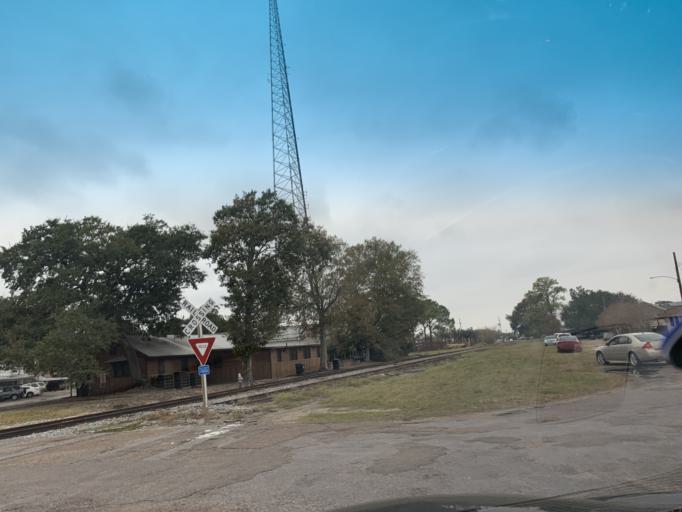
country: US
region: Louisiana
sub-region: Orleans Parish
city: New Orleans
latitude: 29.9847
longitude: -90.1078
